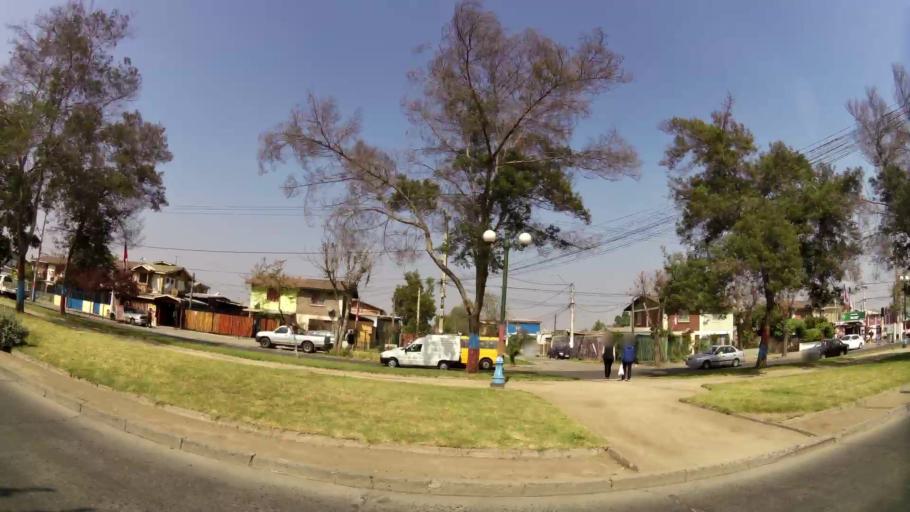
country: CL
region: Santiago Metropolitan
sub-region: Provincia de Santiago
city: Villa Presidente Frei, Nunoa, Santiago, Chile
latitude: -33.4738
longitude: -70.5915
